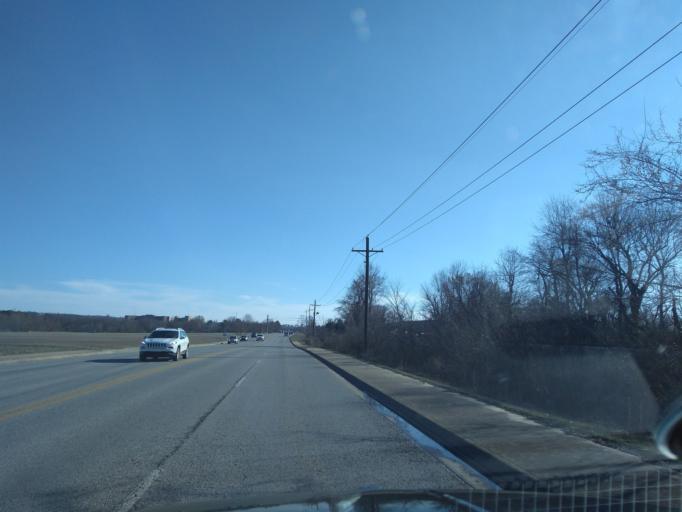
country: US
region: Arkansas
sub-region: Washington County
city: Johnson
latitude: 36.1212
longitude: -94.1637
